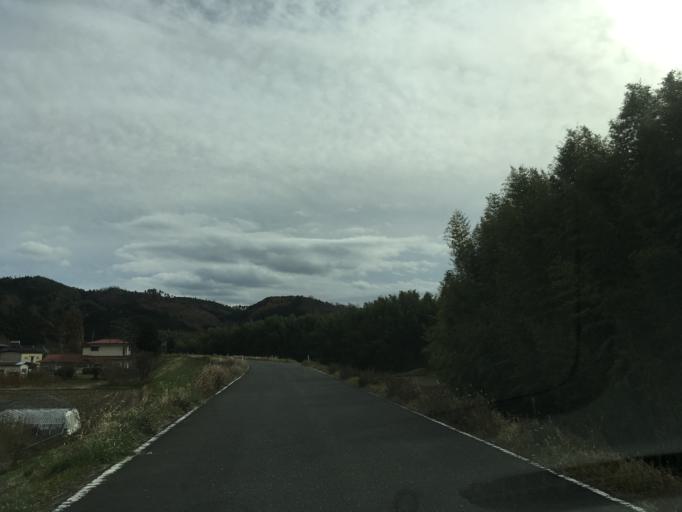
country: JP
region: Iwate
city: Ichinoseki
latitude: 38.7559
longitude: 141.2793
